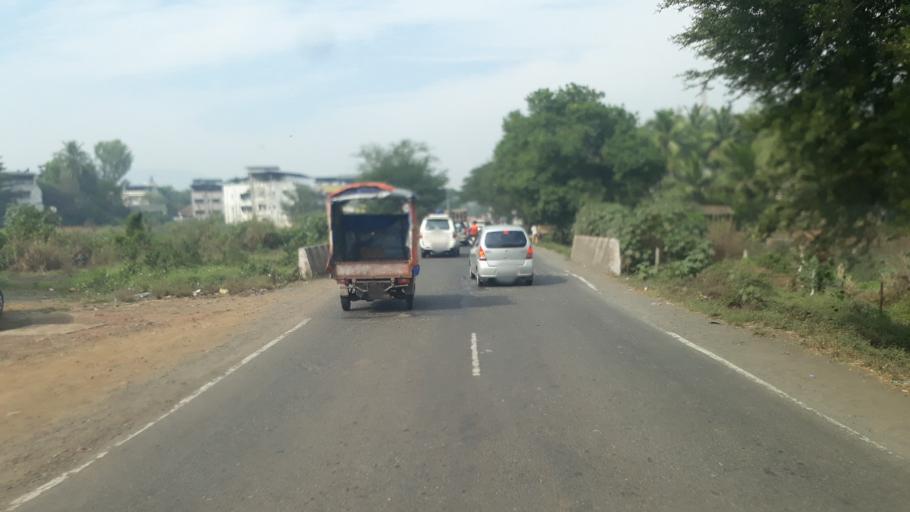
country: IN
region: Maharashtra
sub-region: Raigarh
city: Pen
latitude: 18.6871
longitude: 72.9952
